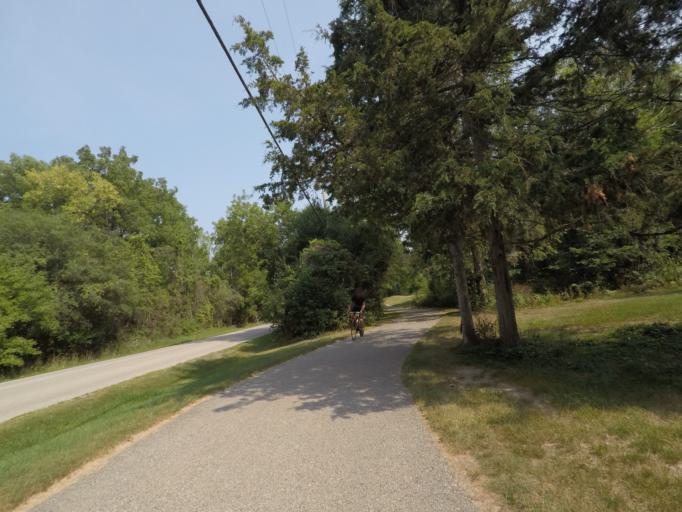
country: US
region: Wisconsin
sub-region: Waukesha County
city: Delafield
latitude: 43.0339
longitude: -88.4142
